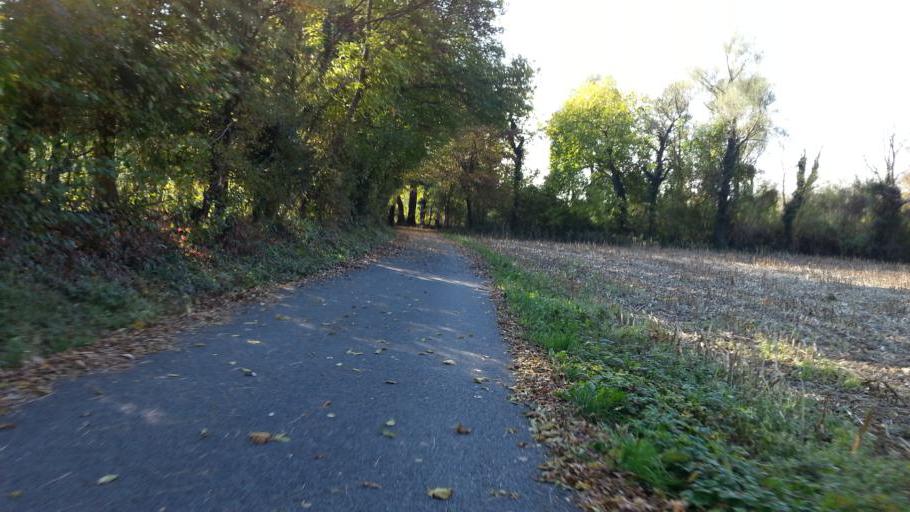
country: IT
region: Friuli Venezia Giulia
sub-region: Provincia di Udine
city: Venzone
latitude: 46.3222
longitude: 13.1280
